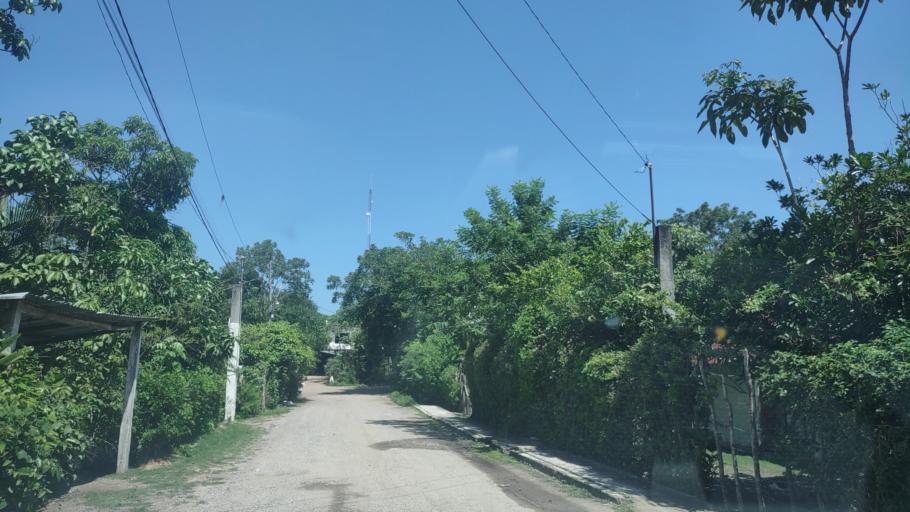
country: MX
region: Veracruz
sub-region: Ozuluama de Mascarenas
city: Cucharas
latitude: 21.5219
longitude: -97.6438
